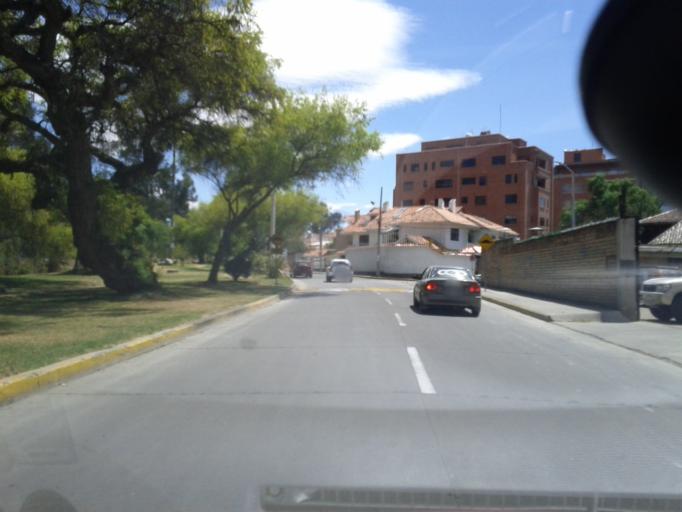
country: EC
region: Azuay
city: Cuenca
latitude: -2.8925
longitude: -79.0218
